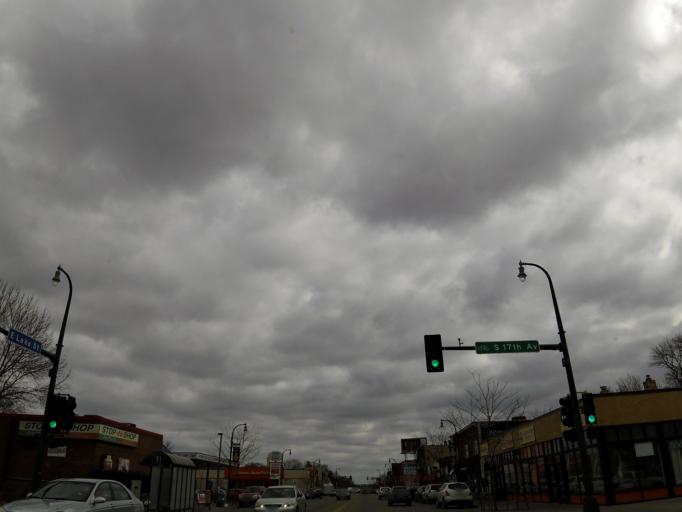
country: US
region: Minnesota
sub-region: Hennepin County
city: Minneapolis
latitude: 44.9484
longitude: -93.2501
